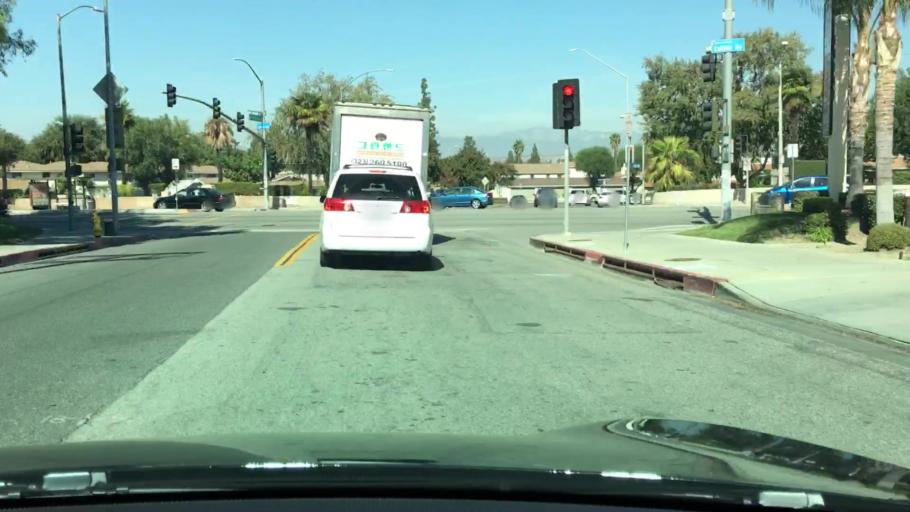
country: US
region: California
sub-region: Los Angeles County
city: Rowland Heights
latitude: 33.9874
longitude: -117.8965
